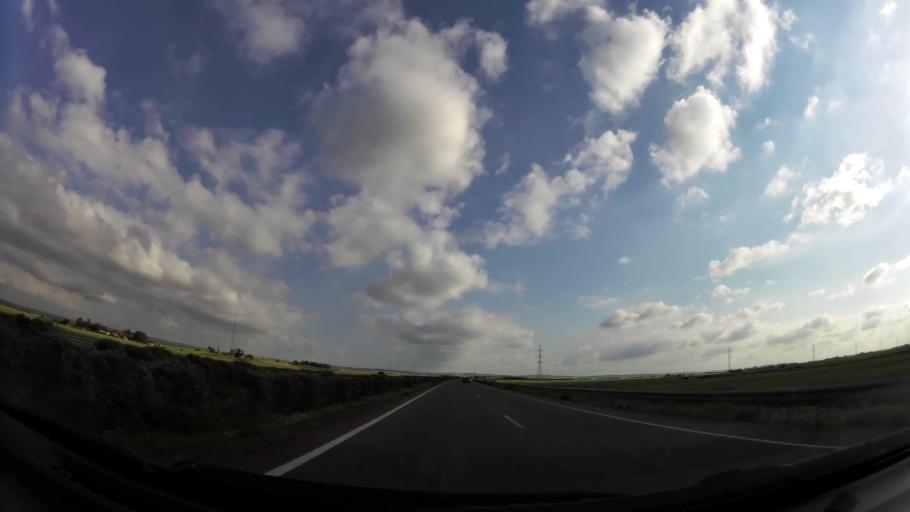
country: MA
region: Chaouia-Ouardigha
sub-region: Settat Province
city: Berrechid
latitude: 33.1587
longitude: -7.5707
